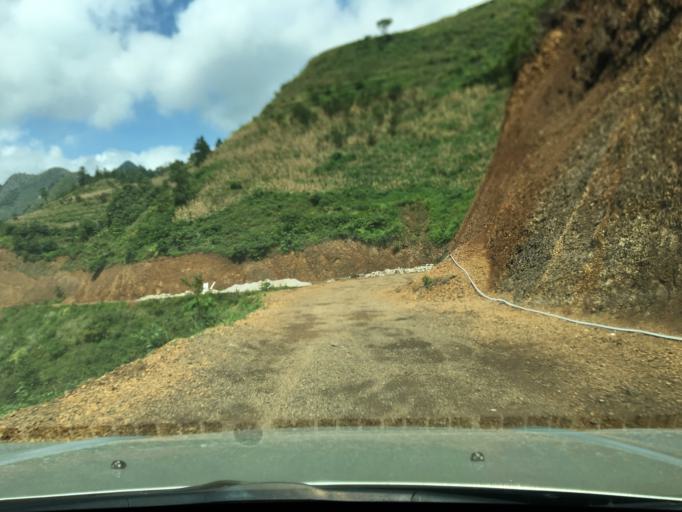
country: CN
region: Guizhou Sheng
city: Liupanshui
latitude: 25.9071
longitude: 105.1119
